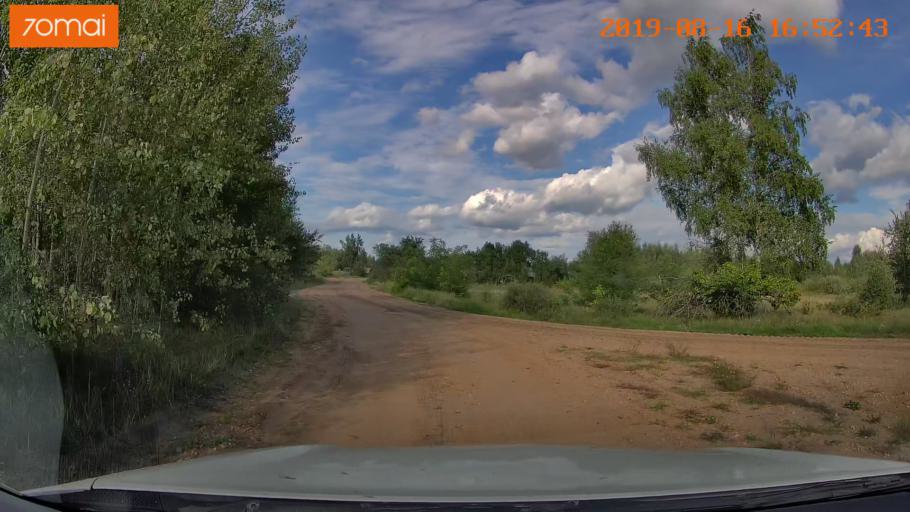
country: BY
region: Mogilev
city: Asipovichy
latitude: 53.2533
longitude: 28.8051
